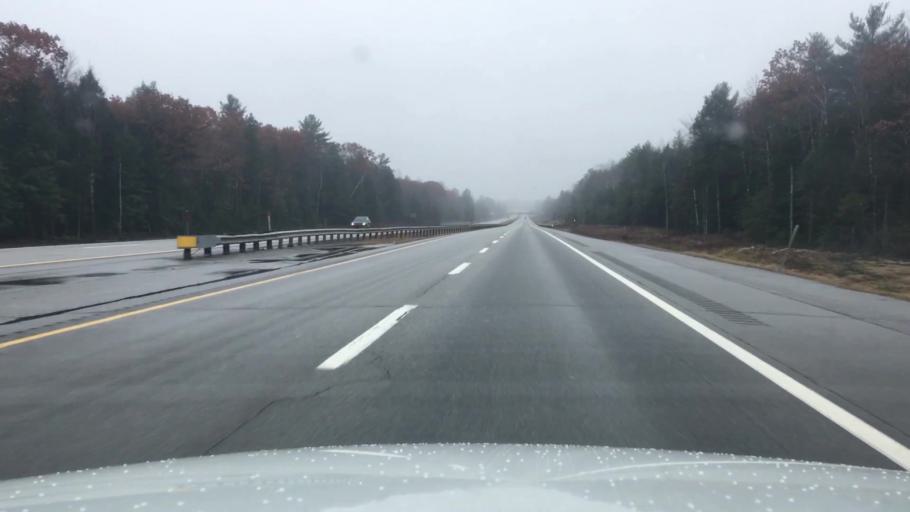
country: US
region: Maine
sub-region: Kennebec County
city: Monmouth
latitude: 44.1365
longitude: -69.9438
